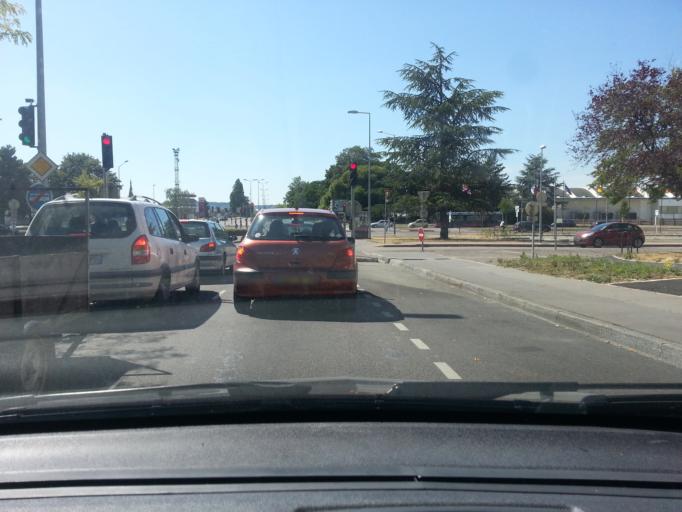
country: FR
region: Bourgogne
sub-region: Departement de la Cote-d'Or
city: Saint-Apollinaire
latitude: 47.3361
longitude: 5.0616
